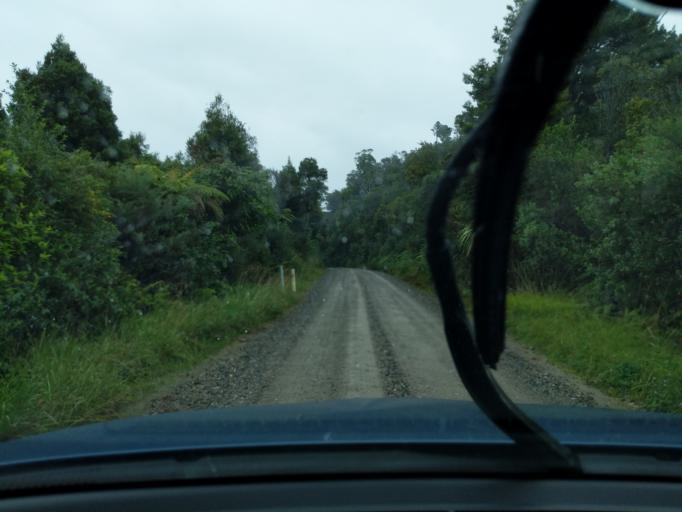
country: NZ
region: Tasman
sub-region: Tasman District
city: Takaka
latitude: -40.6476
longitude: 172.4709
